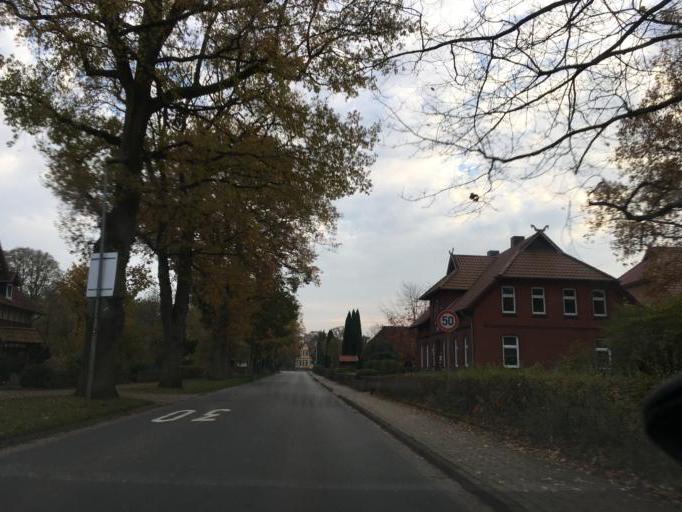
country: DE
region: Lower Saxony
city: Wietzendorf
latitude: 52.9165
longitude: 9.9766
